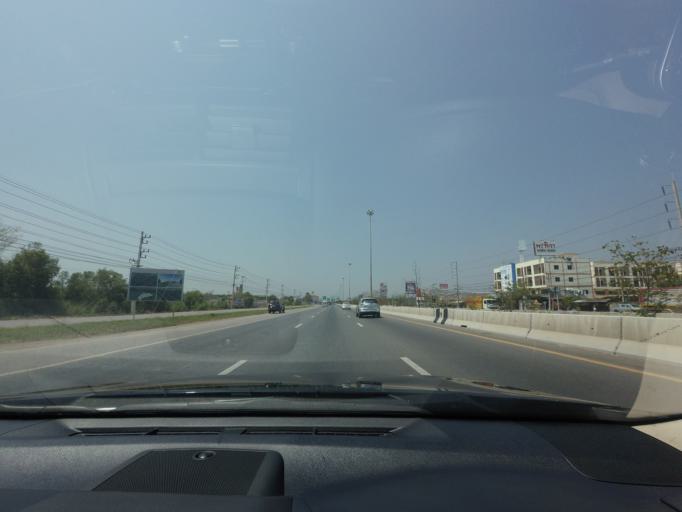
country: TH
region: Samut Songkhram
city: Samut Songkhram
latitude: 13.4054
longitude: 100.0152
